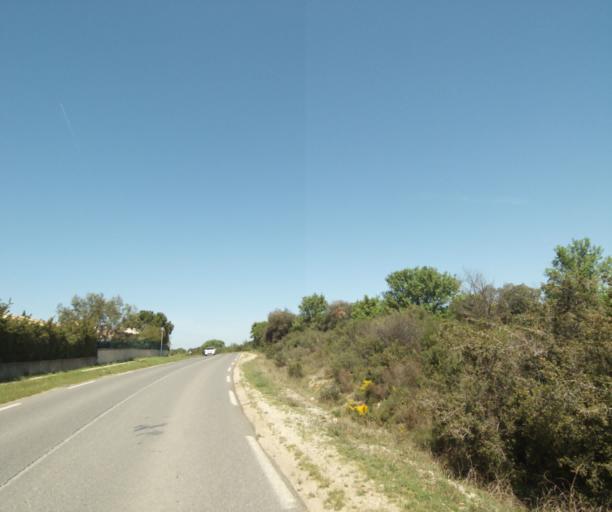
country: FR
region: Languedoc-Roussillon
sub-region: Departement de l'Herault
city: Saint-Bres
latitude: 43.6699
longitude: 4.0358
